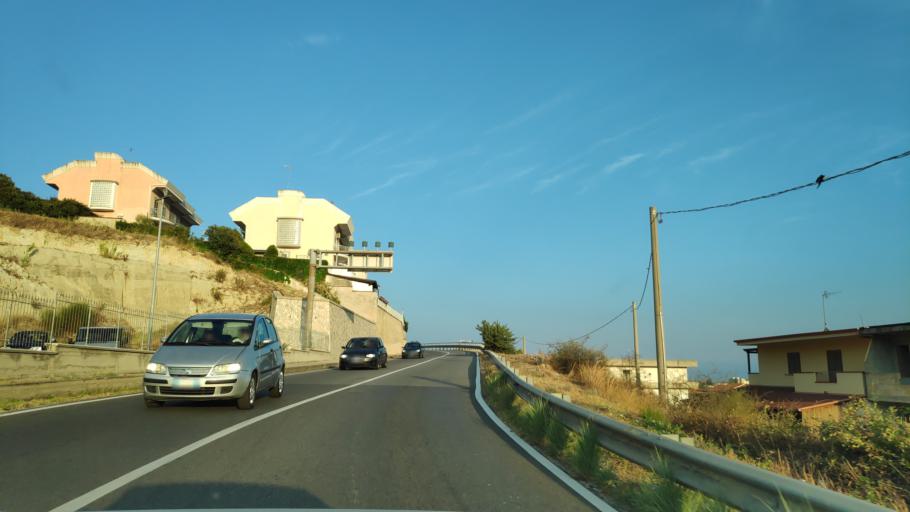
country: IT
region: Calabria
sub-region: Provincia di Catanzaro
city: Martelli-Laganosa
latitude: 38.6791
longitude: 16.5362
